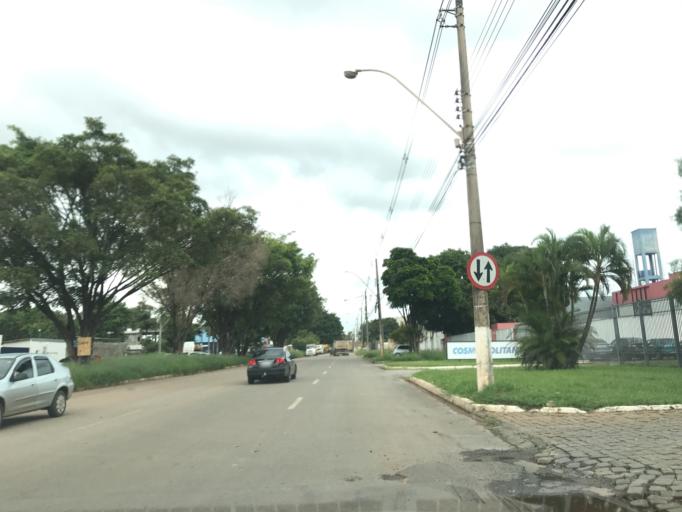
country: BR
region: Federal District
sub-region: Brasilia
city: Brasilia
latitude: -15.7909
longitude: -47.9847
